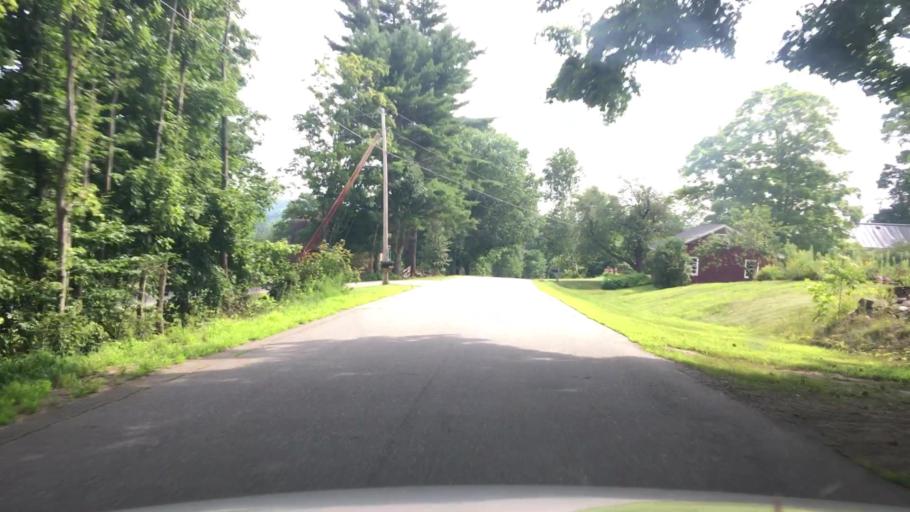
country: US
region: Maine
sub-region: Lincoln County
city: Jefferson
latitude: 44.2272
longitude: -69.4456
